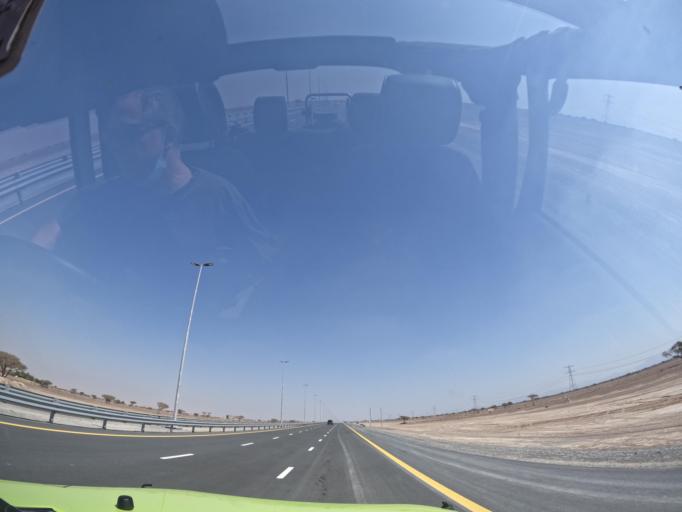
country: AE
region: Ash Shariqah
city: Adh Dhayd
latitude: 24.9445
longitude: 55.8306
